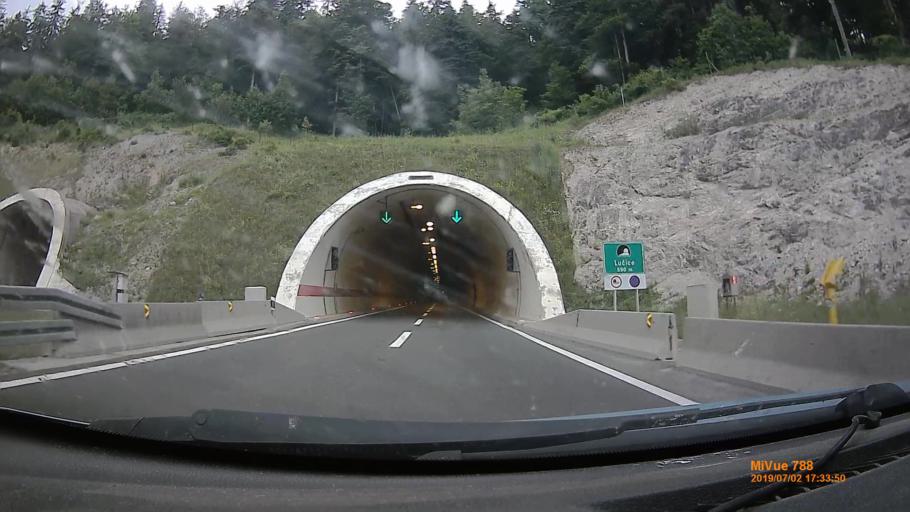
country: HR
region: Primorsko-Goranska
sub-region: Grad Delnice
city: Delnice
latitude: 45.3825
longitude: 14.8016
